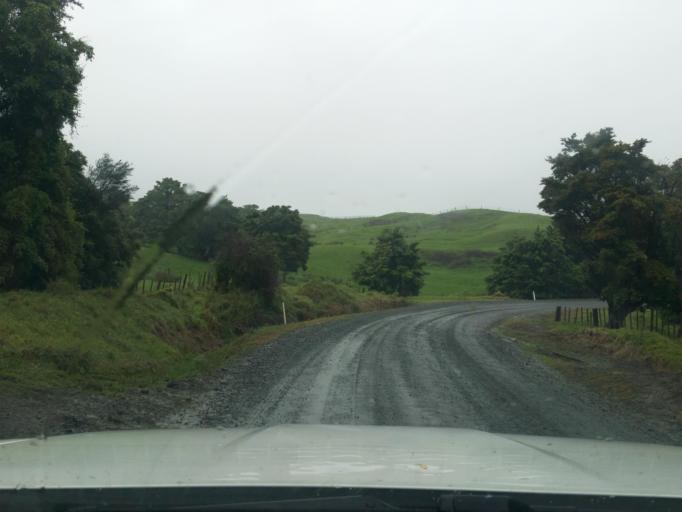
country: NZ
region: Northland
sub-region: Kaipara District
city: Dargaville
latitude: -35.7701
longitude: 173.9610
